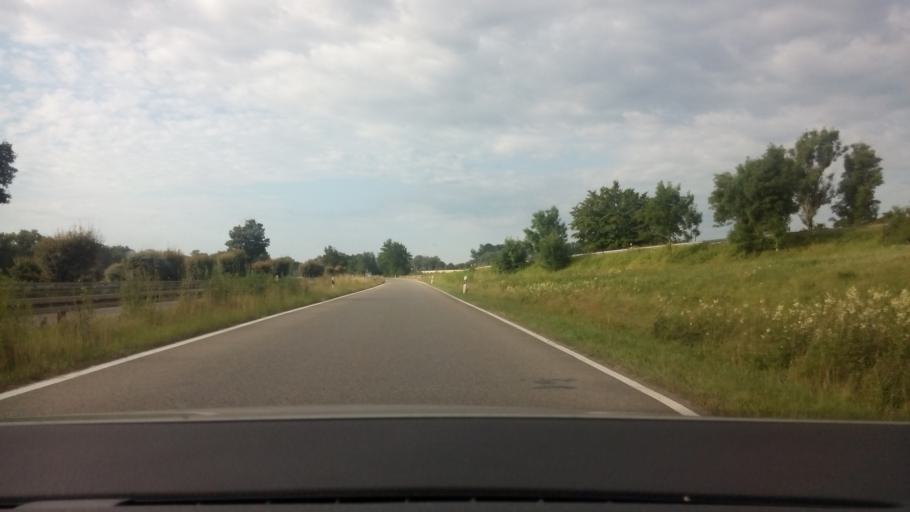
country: DE
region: Bavaria
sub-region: Upper Bavaria
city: Dachau
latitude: 48.2395
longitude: 11.4516
